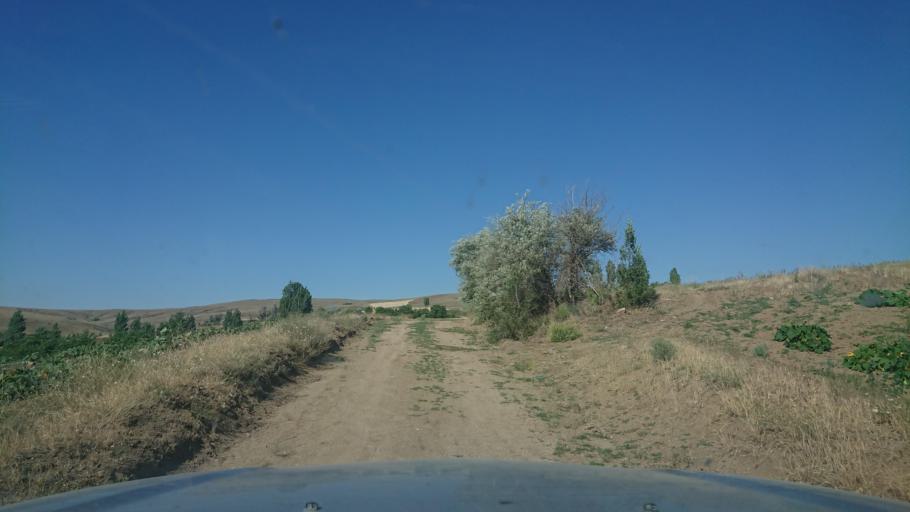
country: TR
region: Aksaray
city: Agacoren
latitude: 38.8463
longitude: 33.9236
